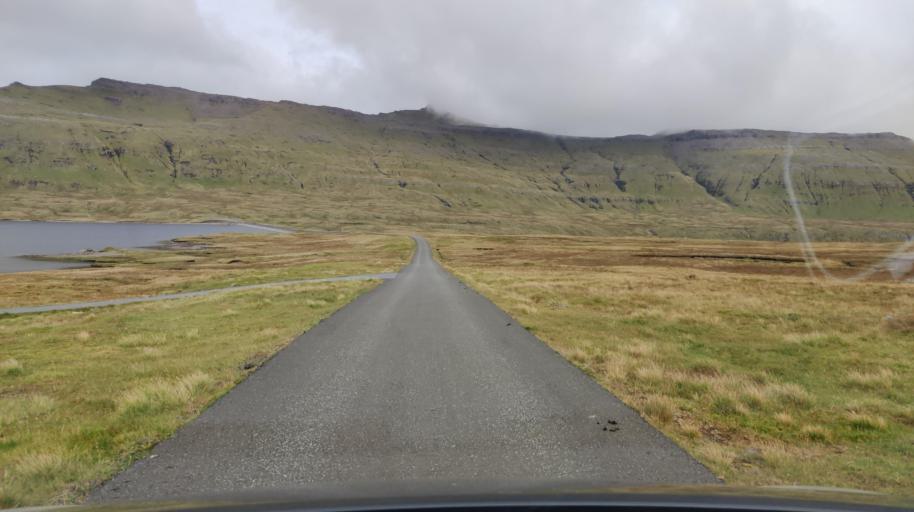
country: FO
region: Streymoy
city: Vestmanna
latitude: 62.1630
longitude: -7.0910
